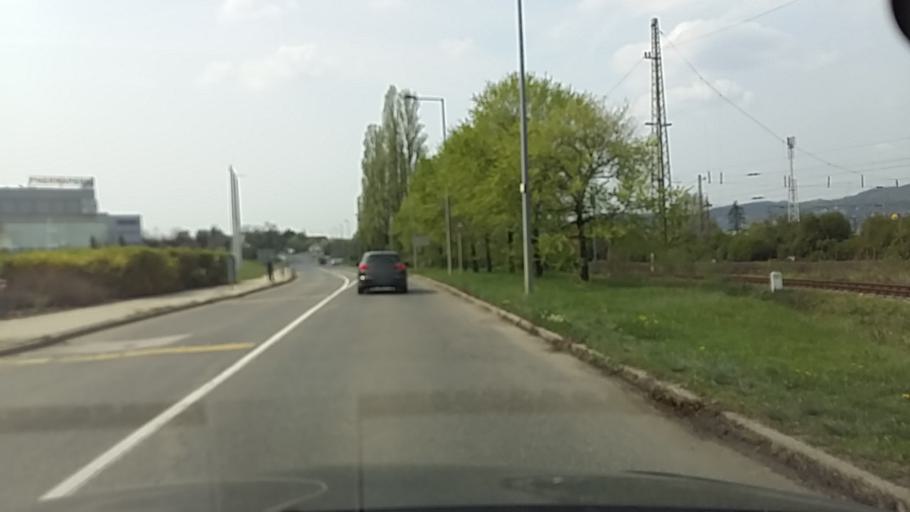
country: HU
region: Pest
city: Budaors
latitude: 47.4469
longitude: 18.9644
